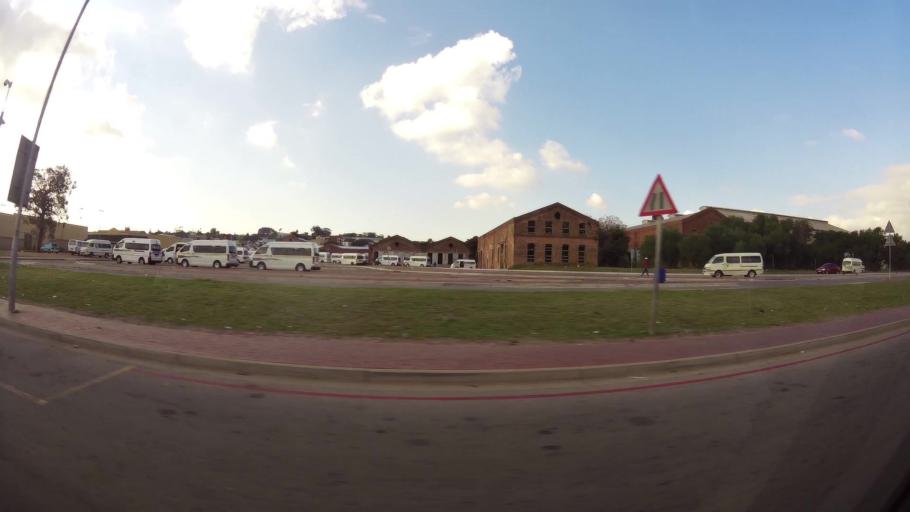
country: ZA
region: Eastern Cape
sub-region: Nelson Mandela Bay Metropolitan Municipality
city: Uitenhage
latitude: -33.7733
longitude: 25.4018
